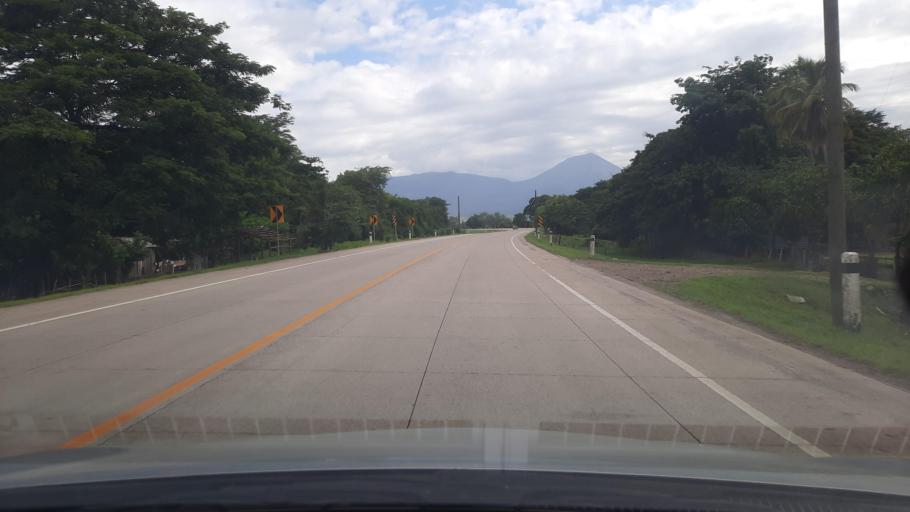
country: NI
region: Chinandega
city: Somotillo
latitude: 12.8172
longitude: -86.8999
